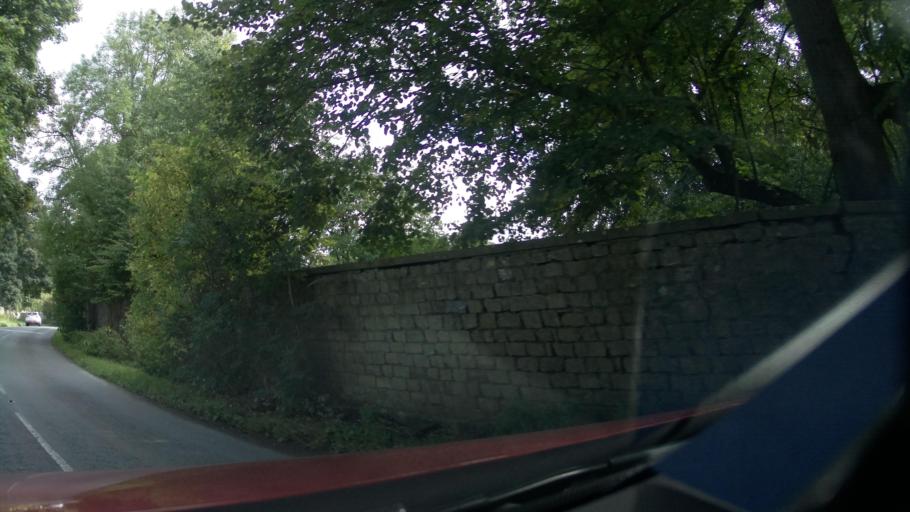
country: GB
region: England
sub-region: North Yorkshire
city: Leyburn
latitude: 54.2680
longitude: -1.7453
